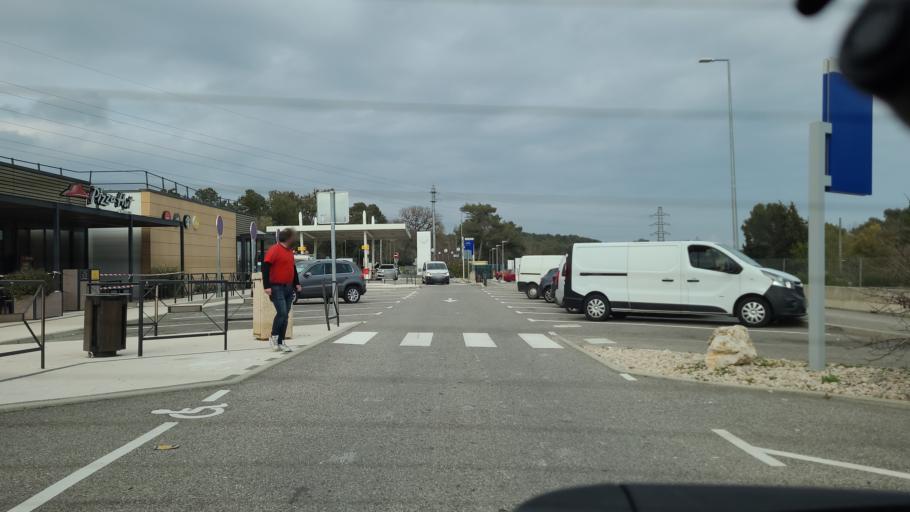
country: FR
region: Provence-Alpes-Cote d'Azur
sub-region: Departement des Alpes-Maritimes
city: Le Cannet
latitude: 43.5915
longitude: 7.0358
